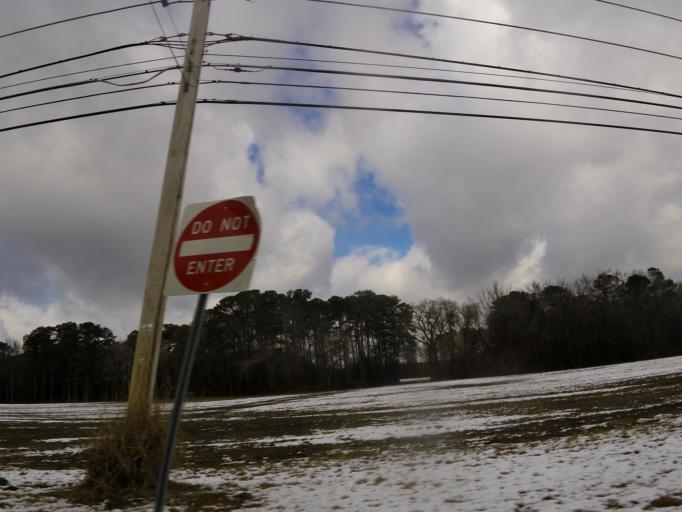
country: US
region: North Carolina
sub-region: Wilson County
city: Lucama
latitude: 35.7036
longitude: -78.0364
